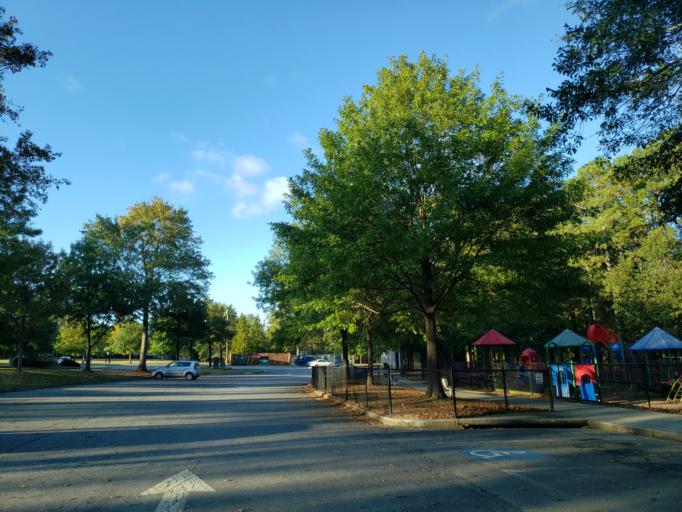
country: US
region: Georgia
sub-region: Cobb County
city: Marietta
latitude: 33.9479
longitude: -84.5723
